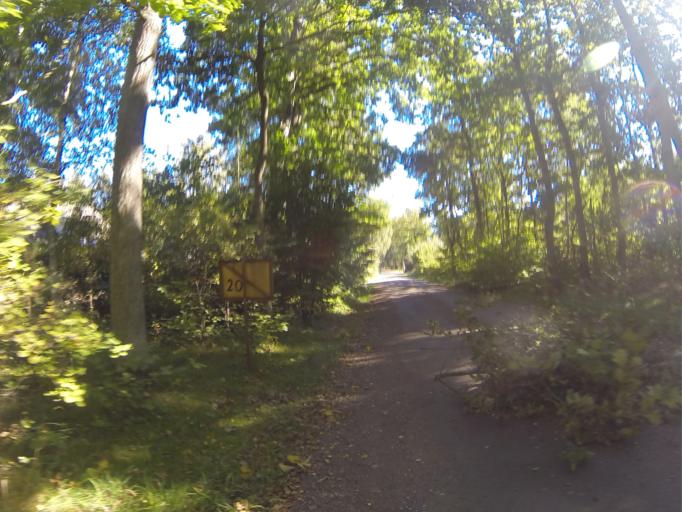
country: SE
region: Skane
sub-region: Hoors Kommun
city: Loberod
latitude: 55.7341
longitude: 13.3994
